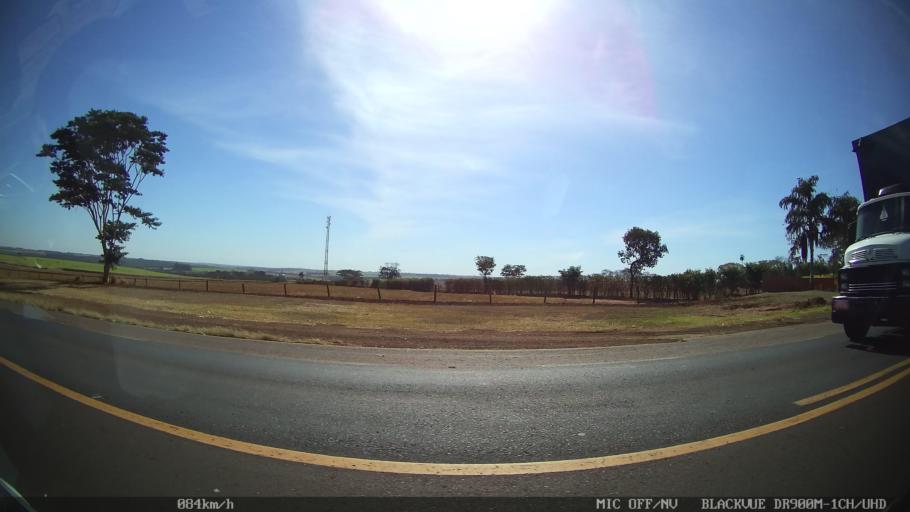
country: BR
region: Sao Paulo
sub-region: Barretos
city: Barretos
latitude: -20.5764
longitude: -48.6818
